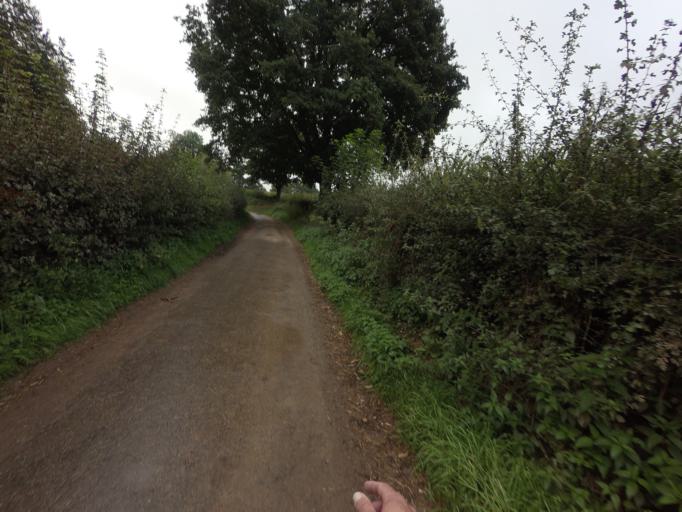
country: NL
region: Limburg
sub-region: Eijsden-Margraten
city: Margraten
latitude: 50.8150
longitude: 5.7741
